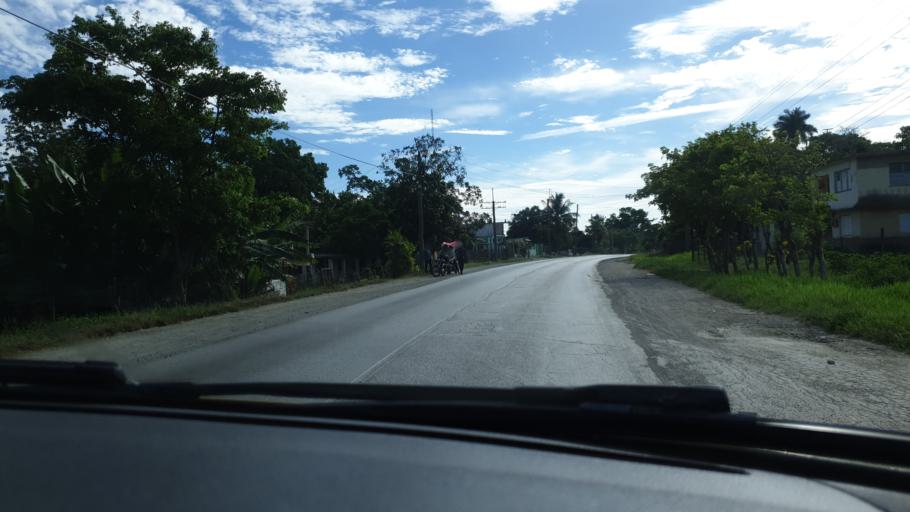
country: CU
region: Villa Clara
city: Santa Clara
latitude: 22.4176
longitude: -79.9422
